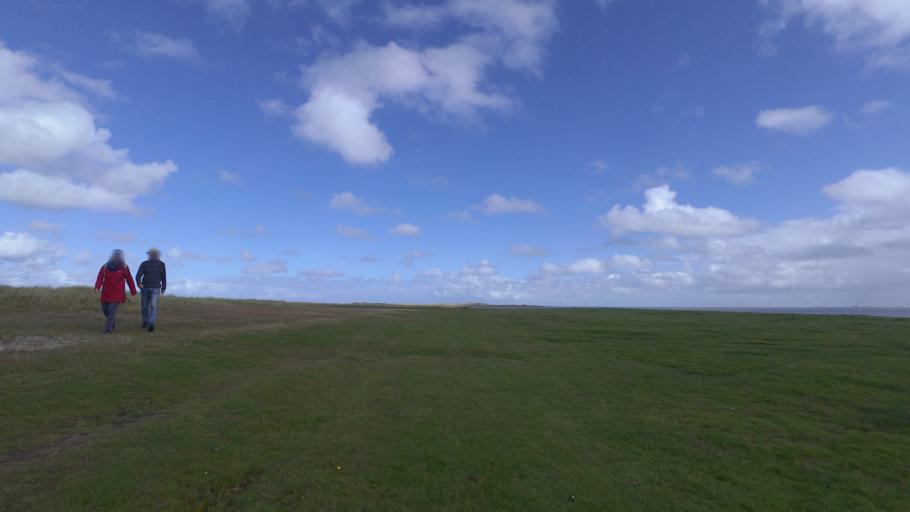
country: NL
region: Friesland
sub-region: Gemeente Dongeradeel
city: Holwerd
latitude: 53.4472
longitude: 5.8621
